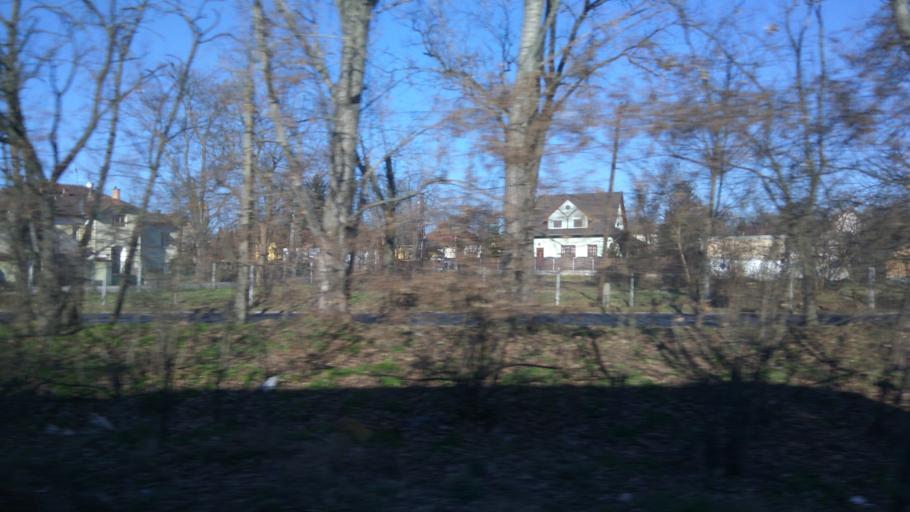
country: HU
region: Budapest
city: Budapest XVII. keruelet
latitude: 47.4876
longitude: 19.2468
